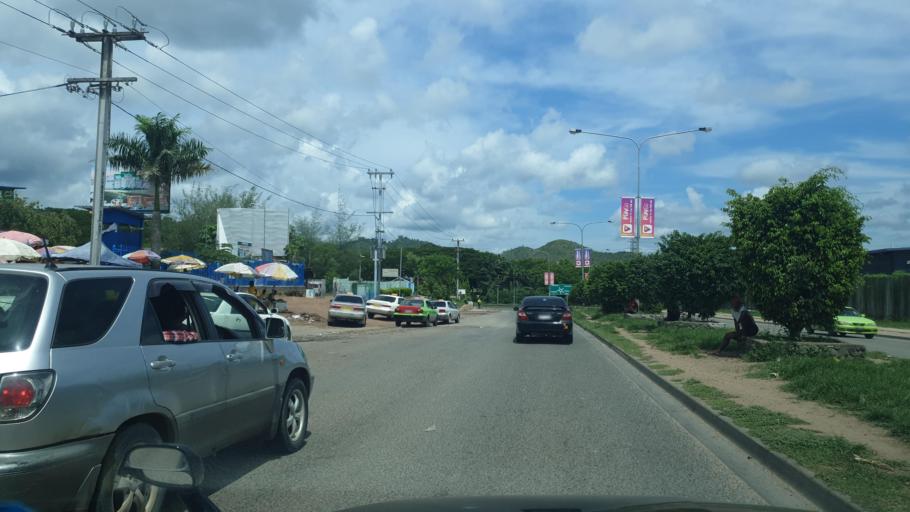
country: PG
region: National Capital
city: Port Moresby
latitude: -9.3999
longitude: 147.1611
